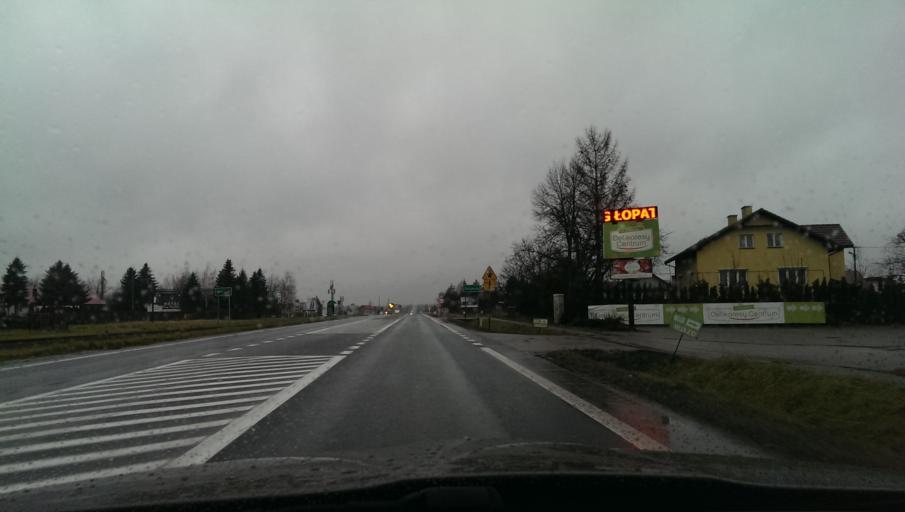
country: PL
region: Subcarpathian Voivodeship
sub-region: Powiat rzeszowski
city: Rudna Mala
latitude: 50.0799
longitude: 21.9859
